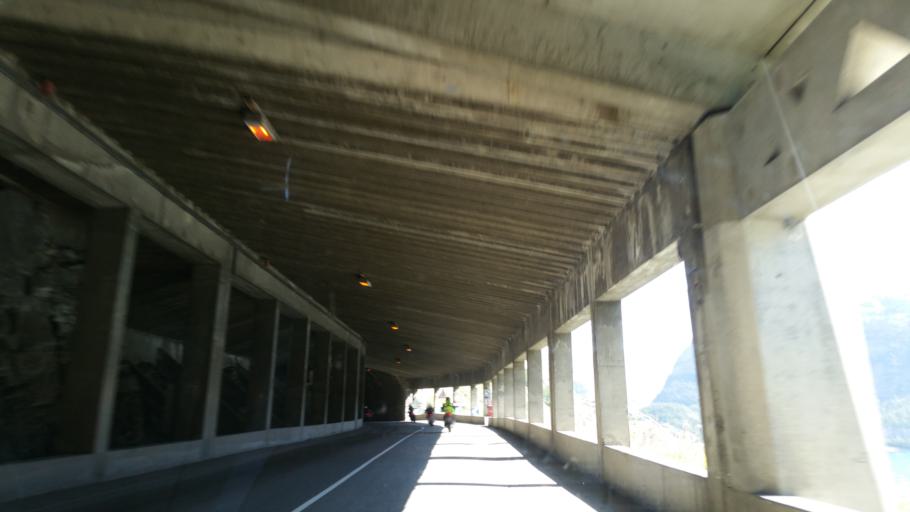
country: FR
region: Rhone-Alpes
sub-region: Departement de la Savoie
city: Tignes
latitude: 45.4944
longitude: 6.9366
